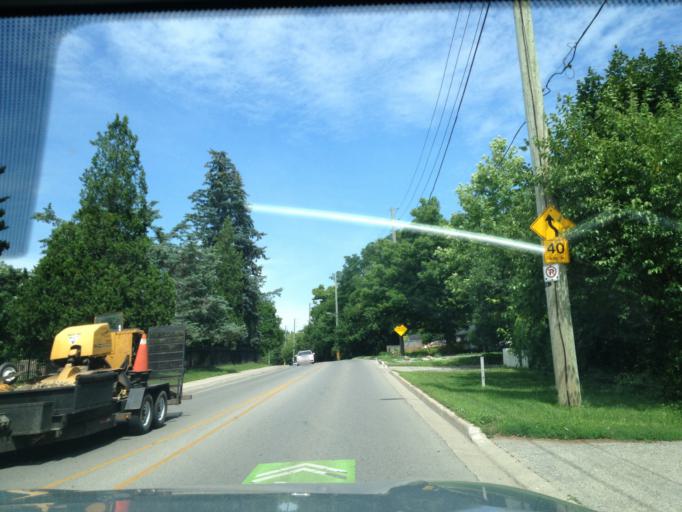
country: CA
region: Ontario
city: London
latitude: 42.9803
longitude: -81.2776
